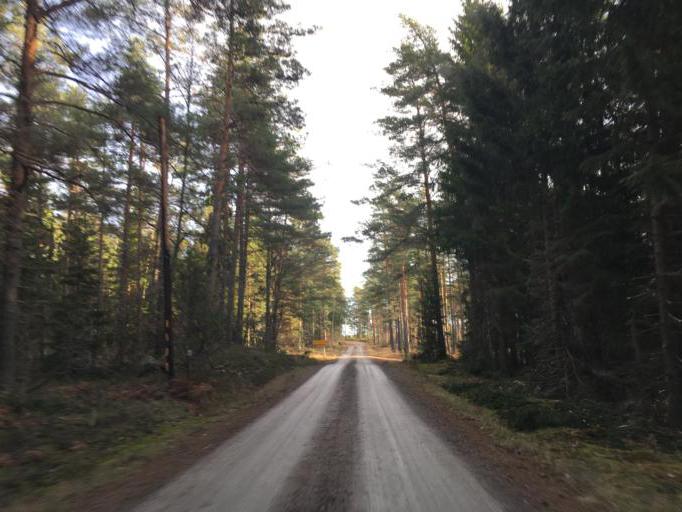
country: SE
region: Kalmar
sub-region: Vasterviks Kommun
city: Vaestervik
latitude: 57.6230
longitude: 16.5544
